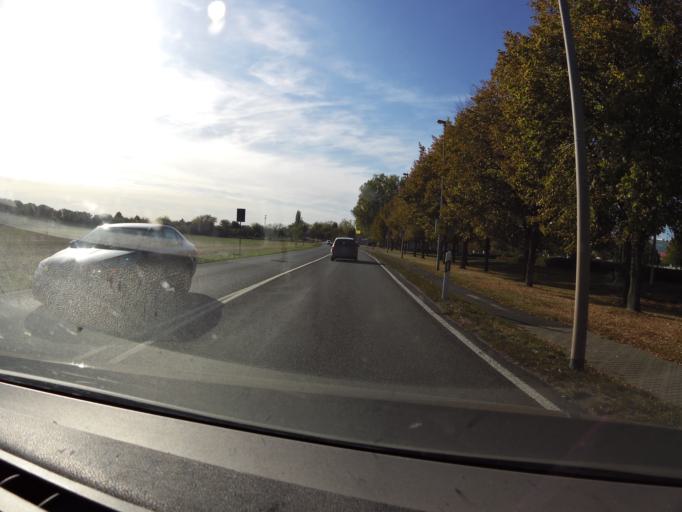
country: DE
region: Saxony-Anhalt
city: Magdeburg
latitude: 52.0822
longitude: 11.6002
